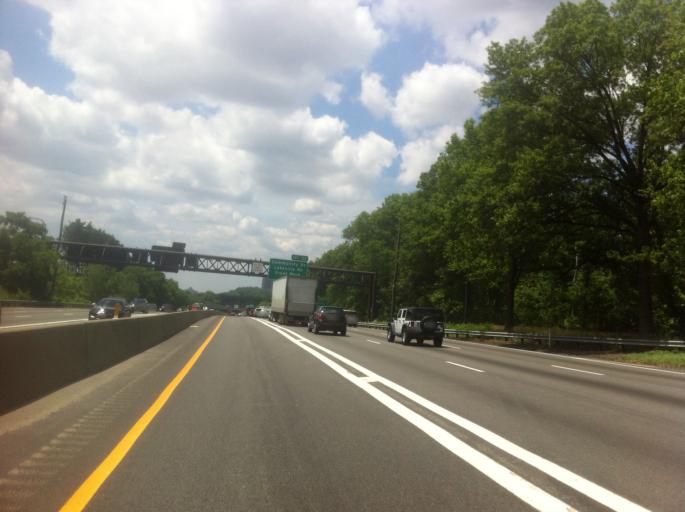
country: US
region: New York
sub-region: Nassau County
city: North Hills
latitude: 40.7740
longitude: -73.6729
